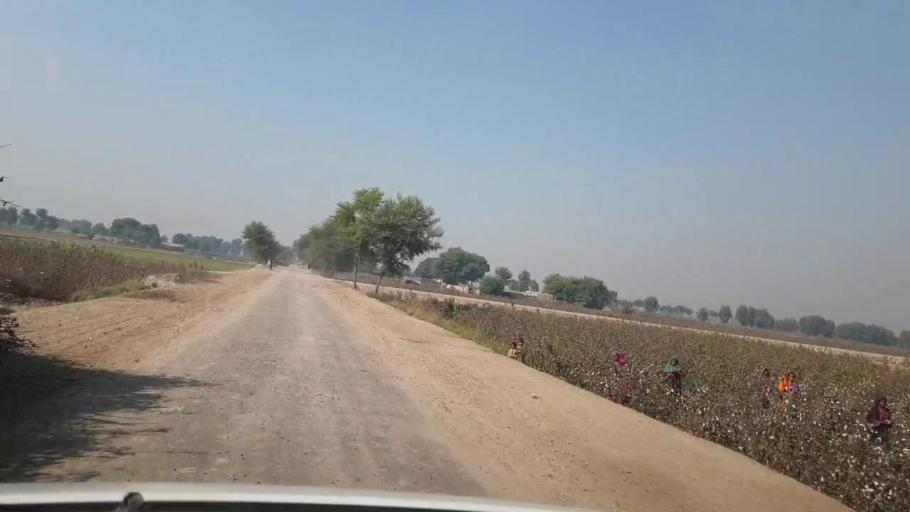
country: PK
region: Sindh
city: Bhan
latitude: 26.6117
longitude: 67.7697
